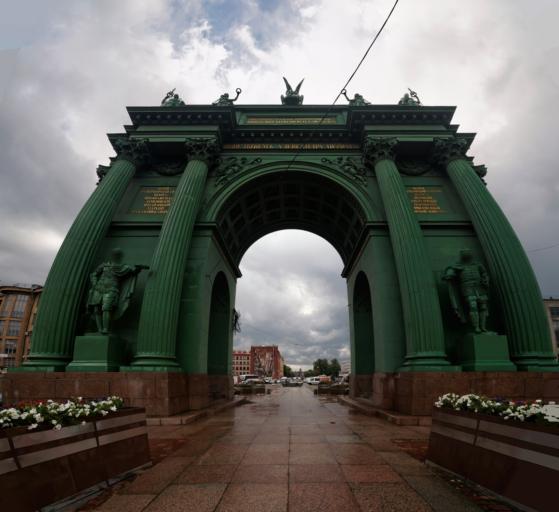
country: RU
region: St.-Petersburg
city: Admiralteisky
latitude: 59.9008
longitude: 30.2739
